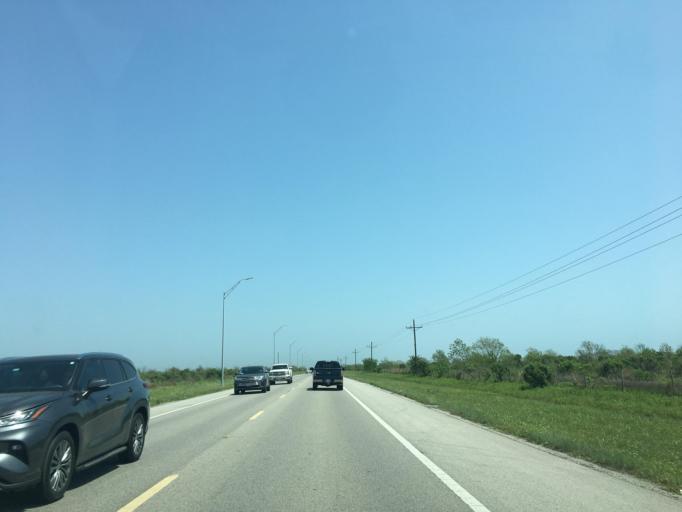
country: US
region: Texas
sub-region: Galveston County
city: Galveston
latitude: 29.3843
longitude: -94.7405
